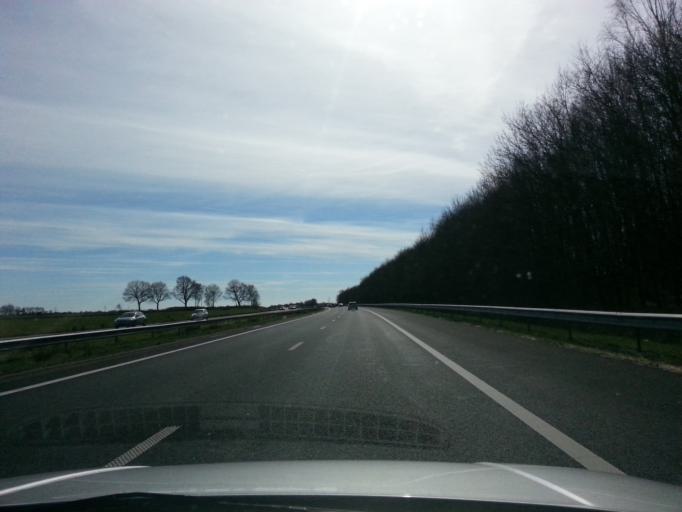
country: NL
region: Drenthe
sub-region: Gemeente Assen
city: Assen
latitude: 52.9183
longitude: 6.5317
